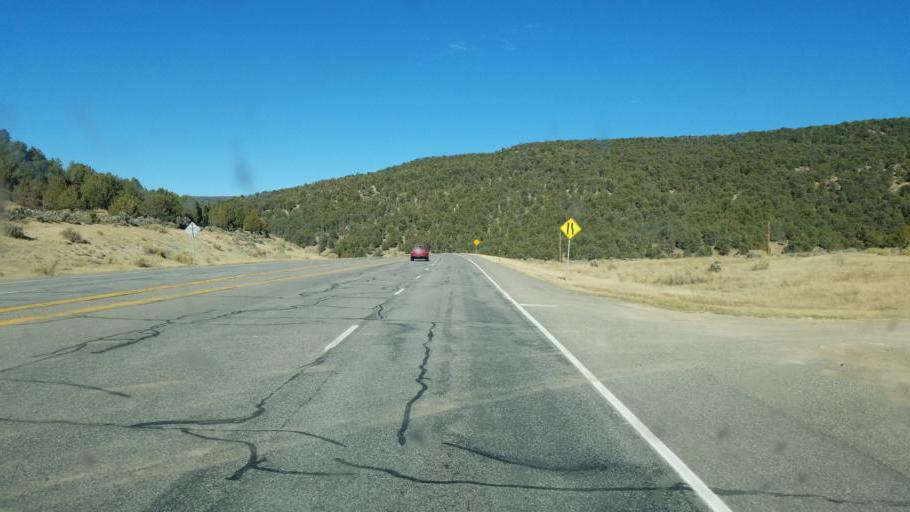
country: US
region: Colorado
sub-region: Ouray County
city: Ouray
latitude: 38.2095
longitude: -107.7288
